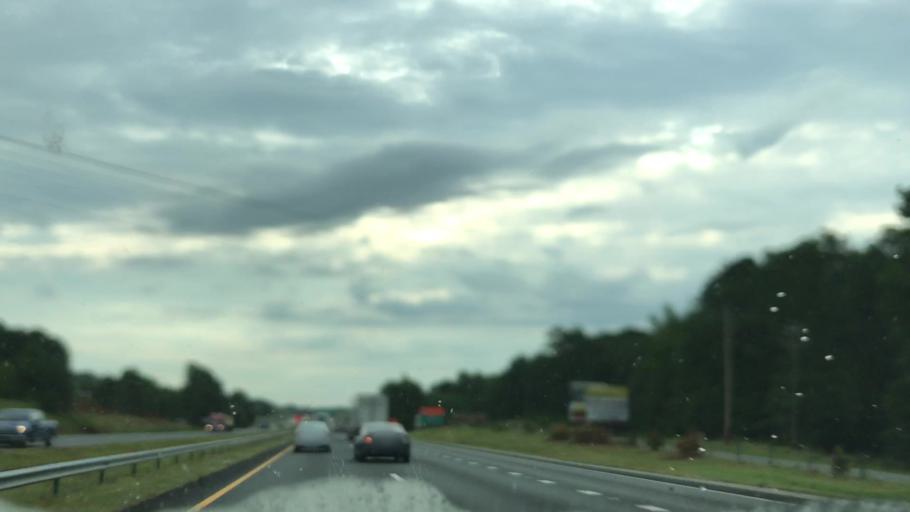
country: US
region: North Carolina
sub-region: Johnston County
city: Benson
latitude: 35.3822
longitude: -78.5304
